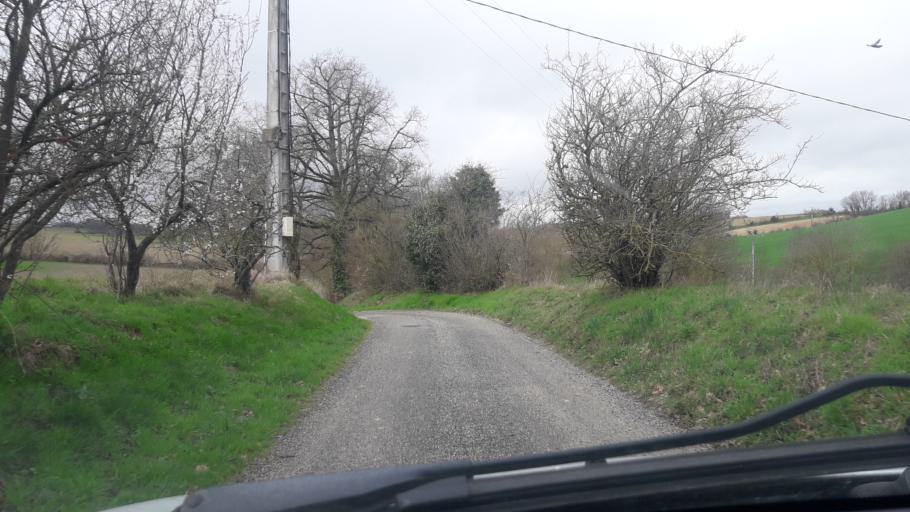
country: FR
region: Midi-Pyrenees
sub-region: Departement du Gers
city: Gimont
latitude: 43.6581
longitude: 0.9565
